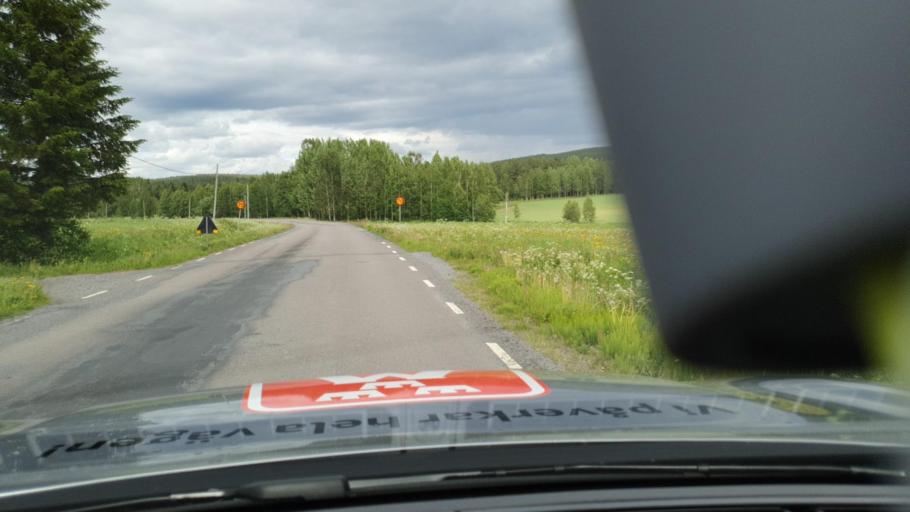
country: SE
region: Norrbotten
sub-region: Lulea Kommun
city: Sodra Sunderbyn
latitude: 65.8521
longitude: 21.9224
